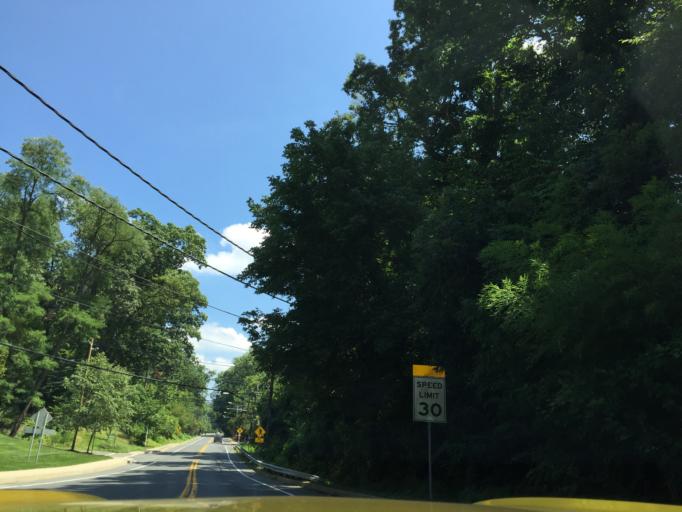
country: US
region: Maryland
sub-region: Montgomery County
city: Cabin John
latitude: 38.9695
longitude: -77.1308
